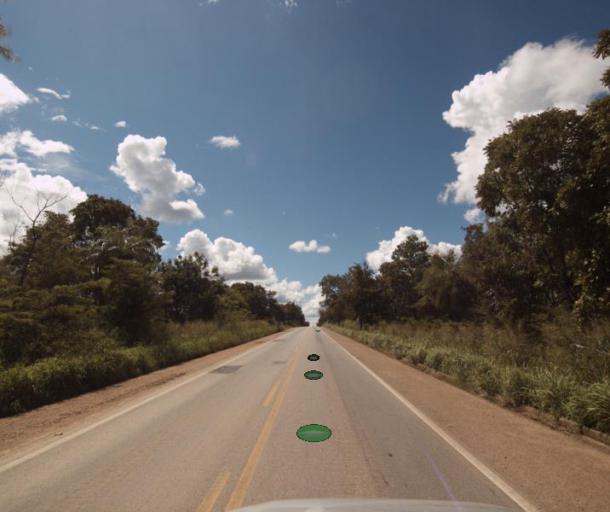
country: BR
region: Goias
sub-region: Porangatu
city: Porangatu
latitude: -13.6953
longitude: -49.0221
